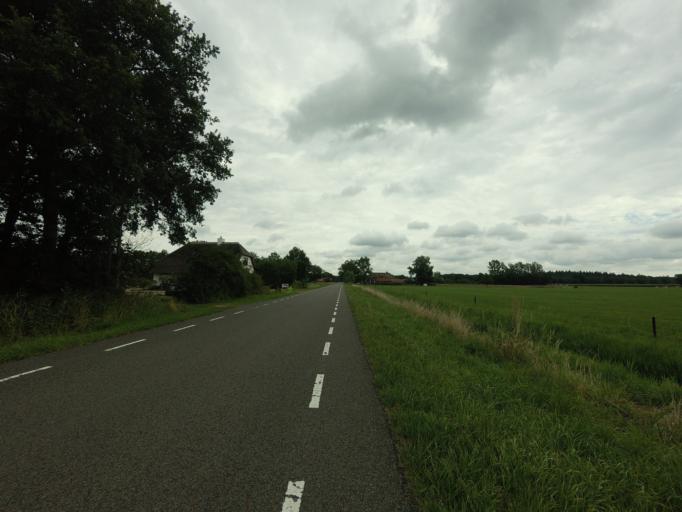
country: NL
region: Gelderland
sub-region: Gemeente Lochem
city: Laren
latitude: 52.2977
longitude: 6.3596
